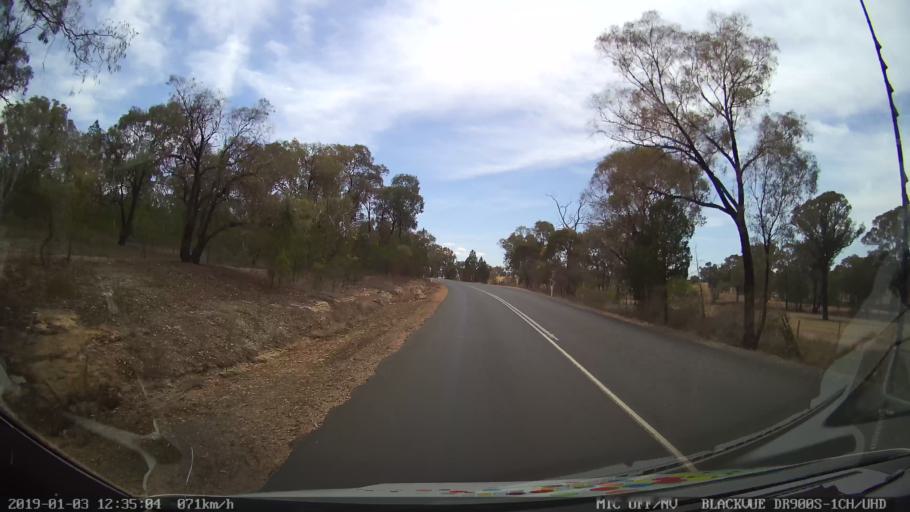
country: AU
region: New South Wales
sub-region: Weddin
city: Grenfell
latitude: -33.8703
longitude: 148.1684
